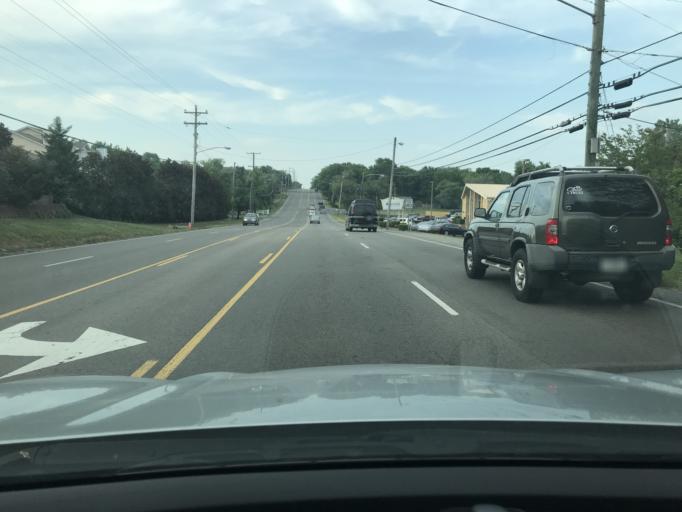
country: US
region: Tennessee
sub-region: Davidson County
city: Goodlettsville
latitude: 36.2996
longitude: -86.7219
